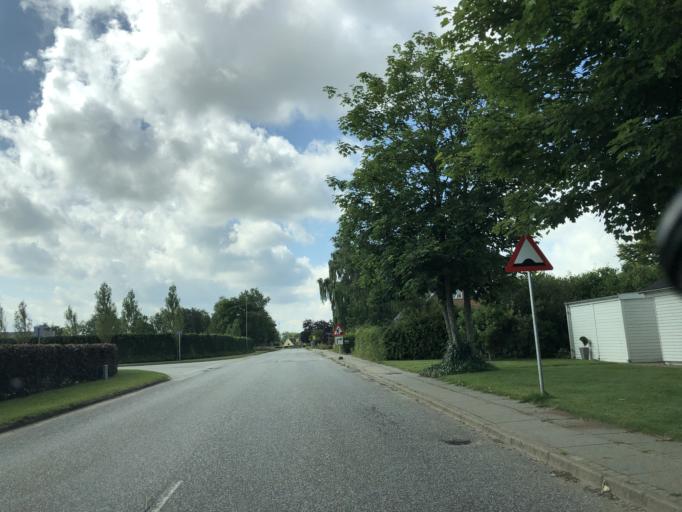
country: DK
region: Central Jutland
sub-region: Ikast-Brande Kommune
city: Brande
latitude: 55.9469
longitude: 9.1378
